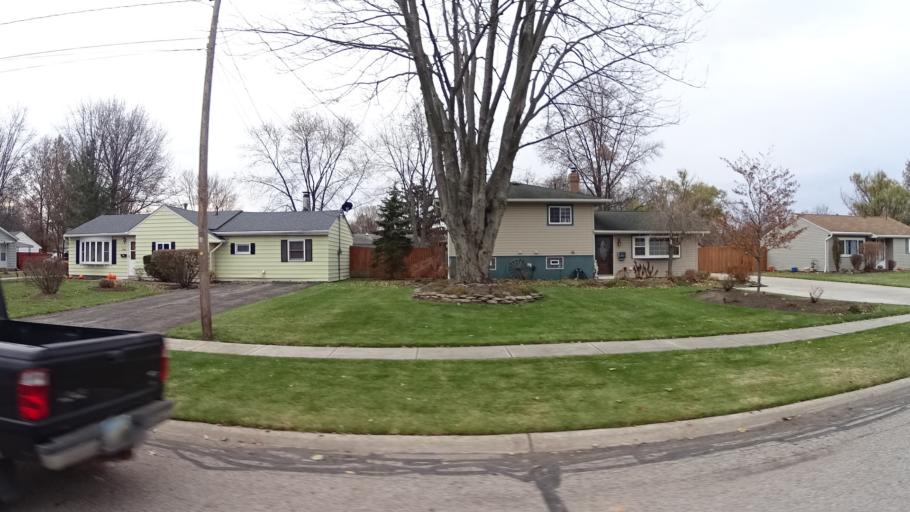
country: US
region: Ohio
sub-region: Lorain County
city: North Ridgeville
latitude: 41.4069
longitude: -82.0036
